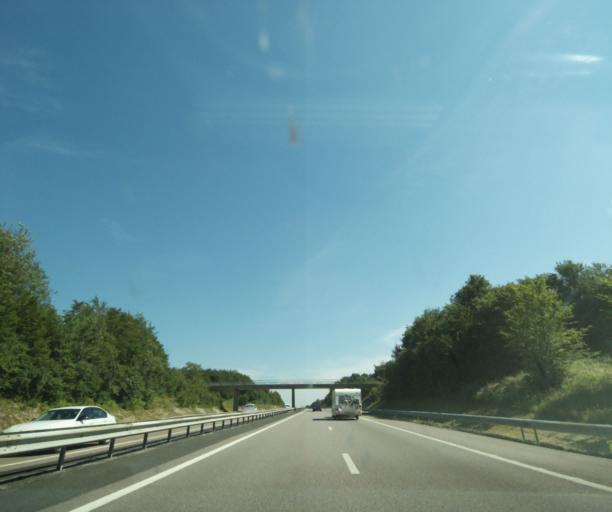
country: FR
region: Lorraine
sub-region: Departement de Meurthe-et-Moselle
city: Colombey-les-Belles
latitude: 48.5009
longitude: 5.9100
